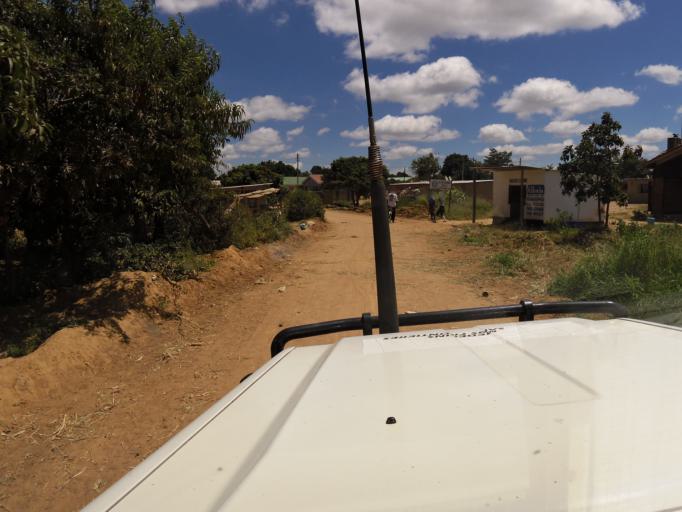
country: ZW
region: Harare
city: Epworth
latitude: -17.9025
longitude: 31.1619
